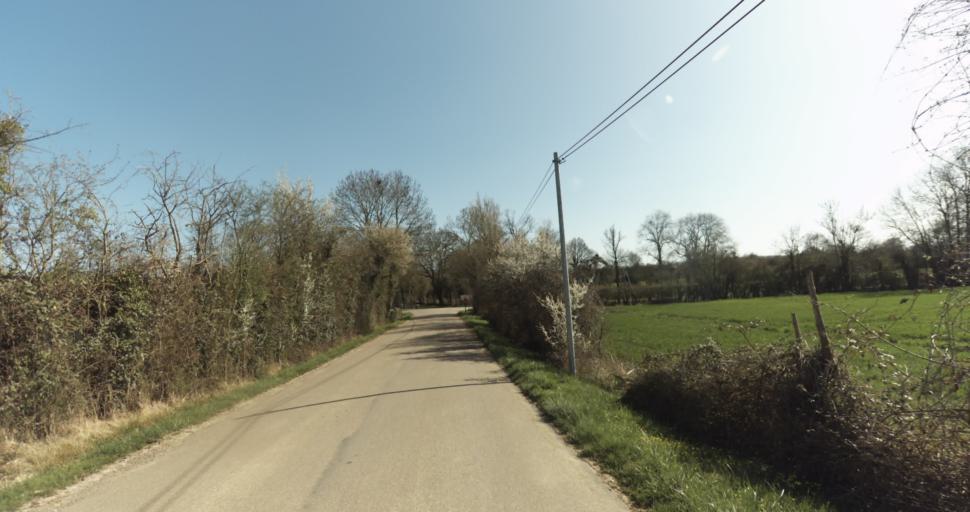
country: FR
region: Lower Normandy
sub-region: Departement du Calvados
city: Saint-Pierre-sur-Dives
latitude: 48.9412
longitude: 0.0190
